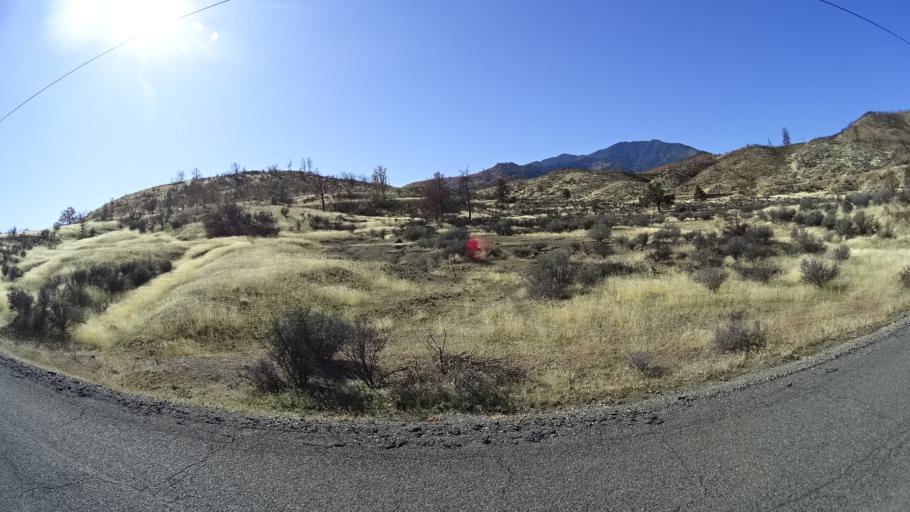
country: US
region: California
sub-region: Siskiyou County
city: Yreka
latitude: 41.9262
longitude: -122.5821
